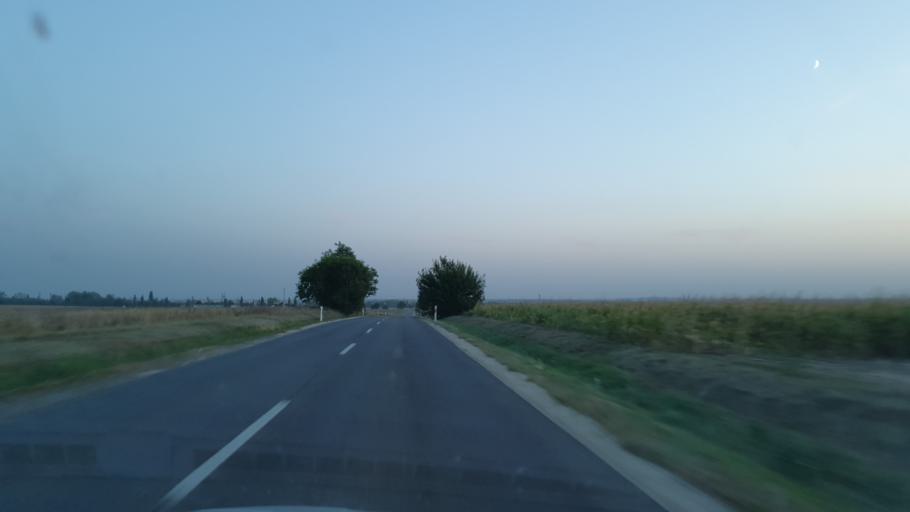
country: HU
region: Fejer
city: Szekesfehervar
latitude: 47.2321
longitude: 18.4165
